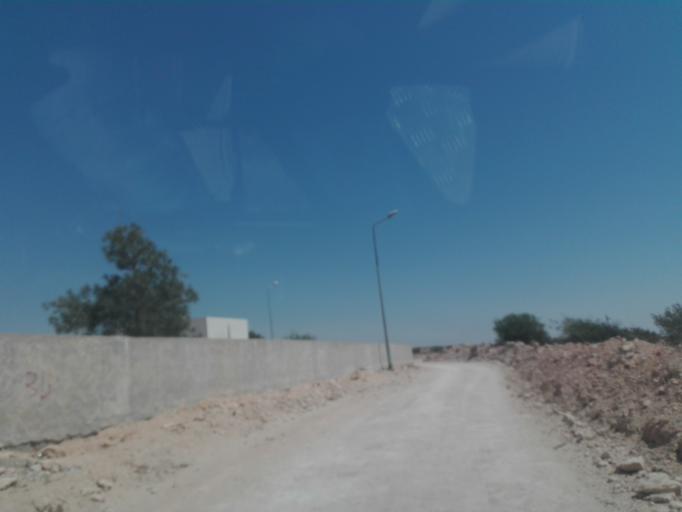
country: TN
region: Safaqis
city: Skhira
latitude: 34.4147
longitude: 9.9513
